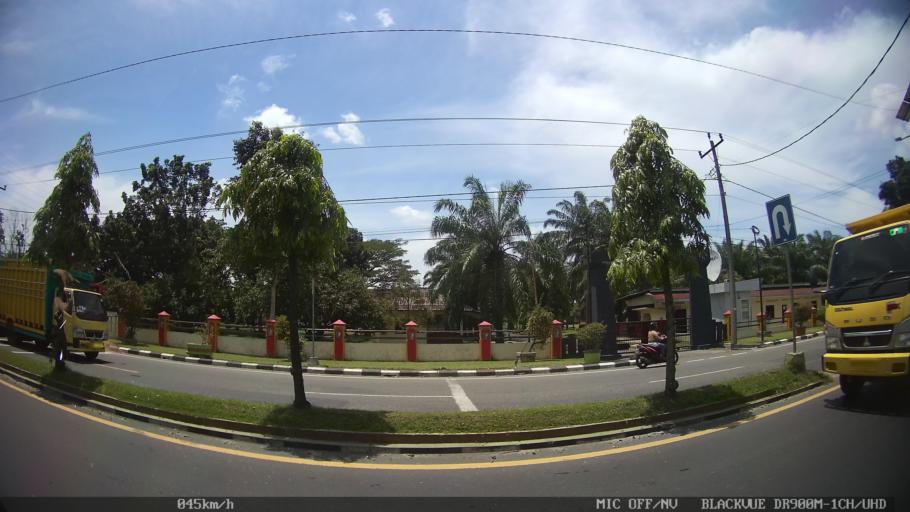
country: ID
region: North Sumatra
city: Binjai
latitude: 3.6086
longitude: 98.5065
